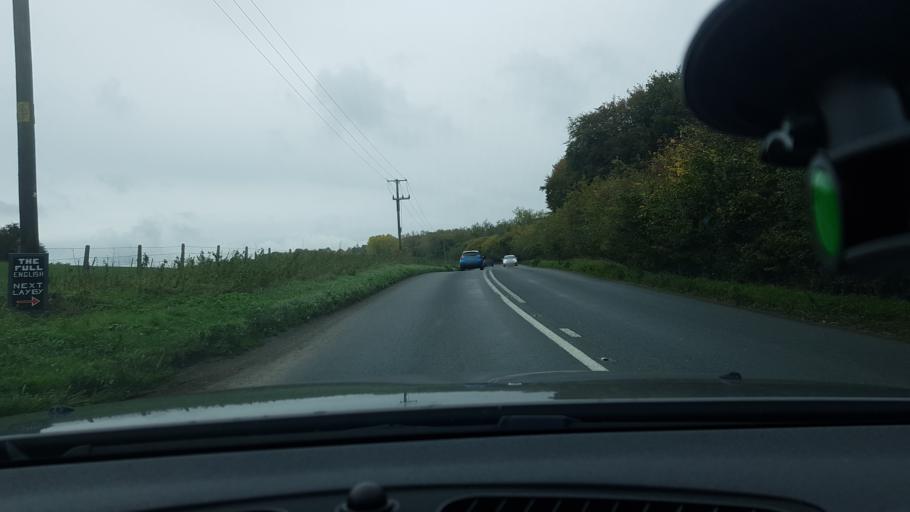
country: GB
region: England
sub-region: Wiltshire
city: Marlborough
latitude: 51.4416
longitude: -1.7313
